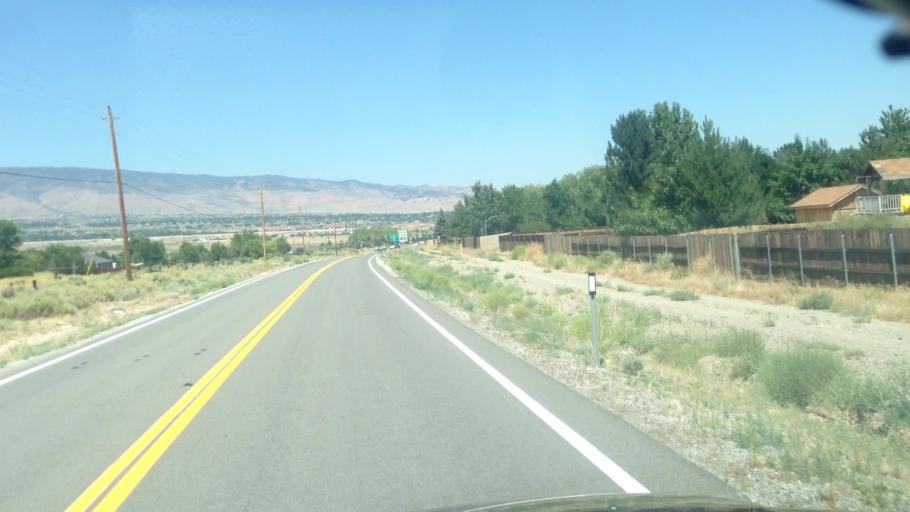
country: US
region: Nevada
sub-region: Storey County
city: Virginia City
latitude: 39.3948
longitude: -119.7295
